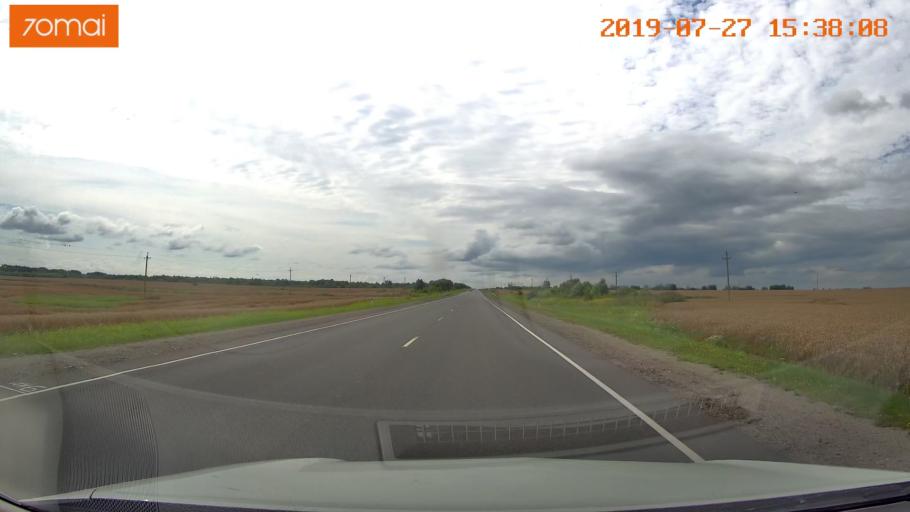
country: RU
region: Kaliningrad
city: Gusev
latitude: 54.6087
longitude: 22.3230
